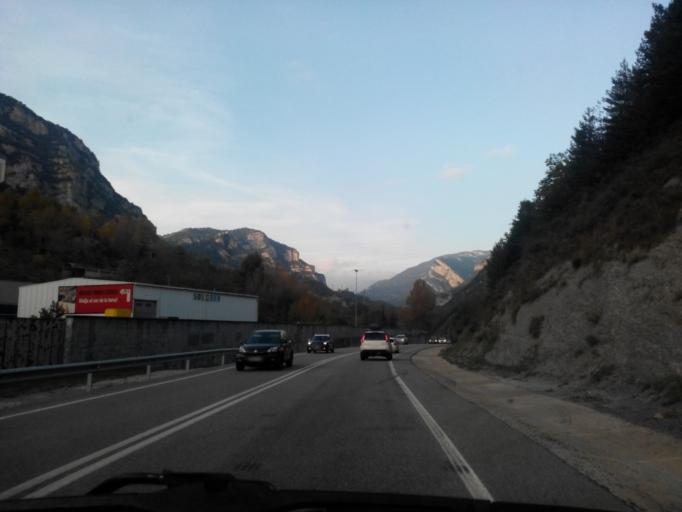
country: ES
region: Catalonia
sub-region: Provincia de Barcelona
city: Vallcebre
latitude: 42.1716
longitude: 1.8603
